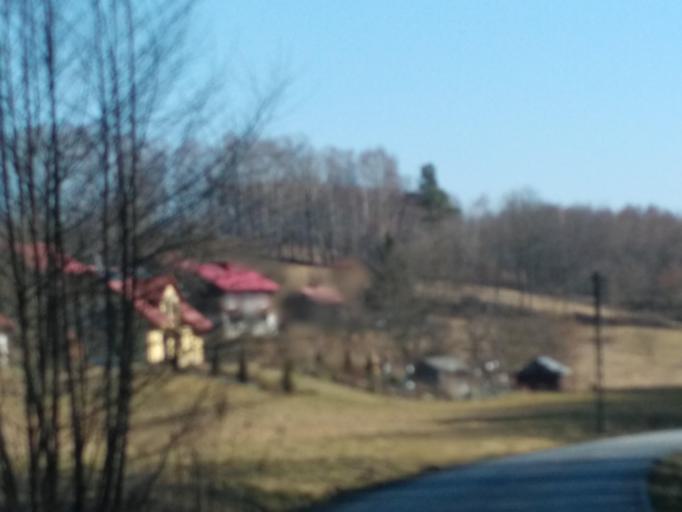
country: PL
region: Subcarpathian Voivodeship
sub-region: Powiat ropczycko-sedziszowski
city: Iwierzyce
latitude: 49.9565
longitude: 21.7338
